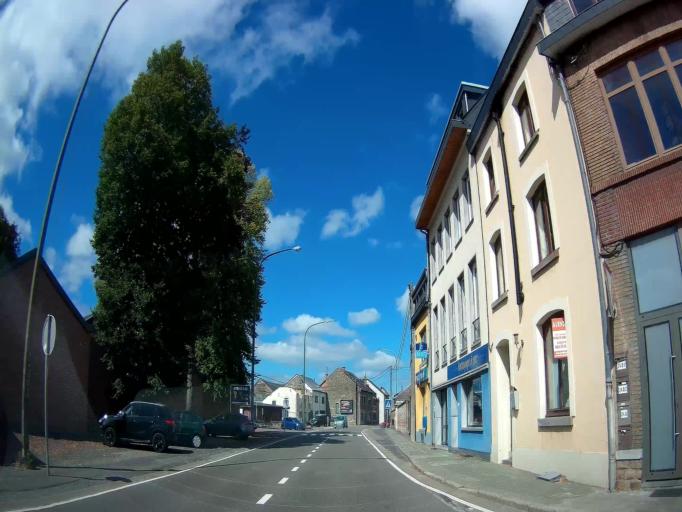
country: BE
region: Wallonia
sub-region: Province du Luxembourg
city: Bastogne
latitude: 50.0071
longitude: 5.7199
